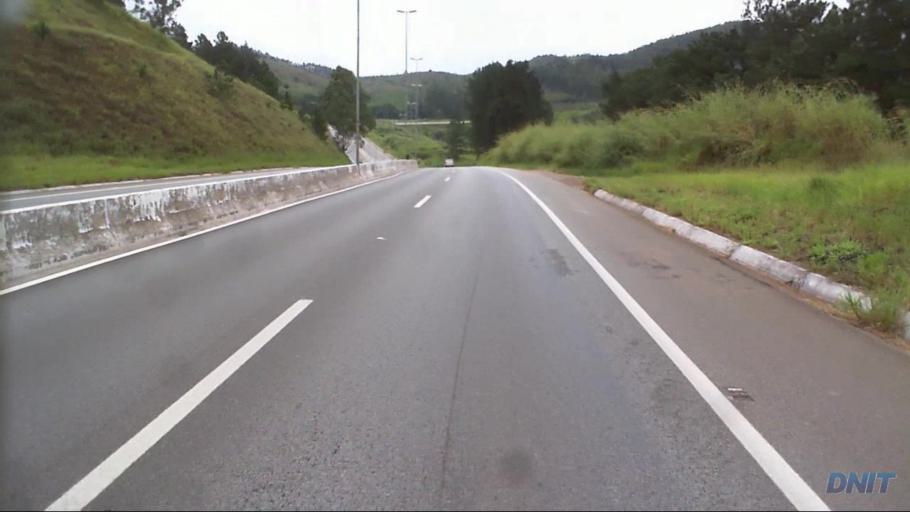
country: BR
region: Minas Gerais
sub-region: Nova Era
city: Nova Era
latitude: -19.7686
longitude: -43.0469
